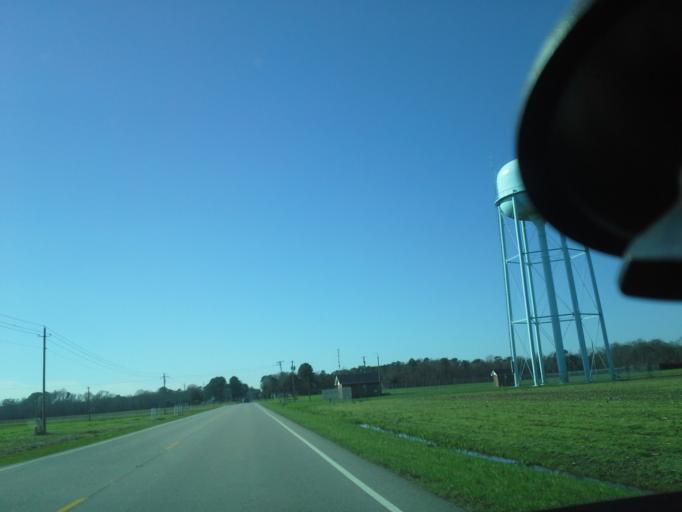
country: US
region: North Carolina
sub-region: Beaufort County
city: Belhaven
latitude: 35.5252
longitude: -76.7976
